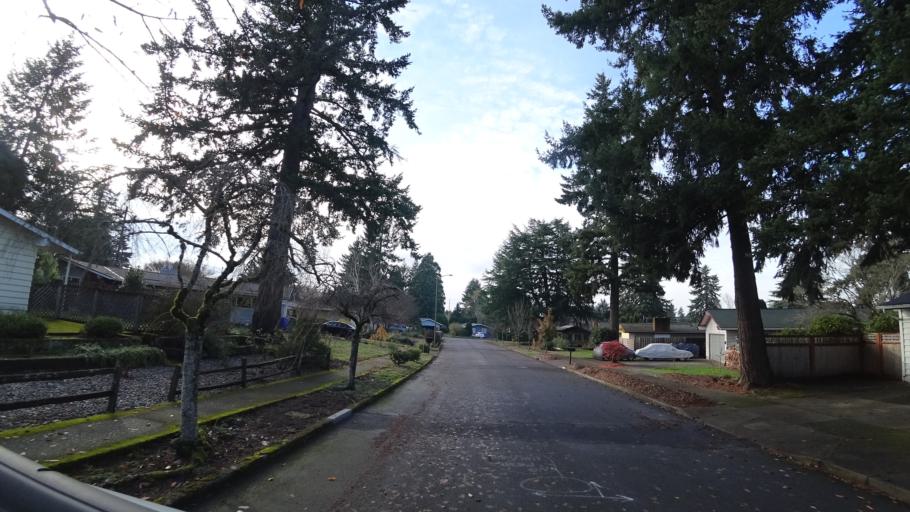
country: US
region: Oregon
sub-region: Multnomah County
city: Lents
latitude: 45.5286
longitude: -122.5282
